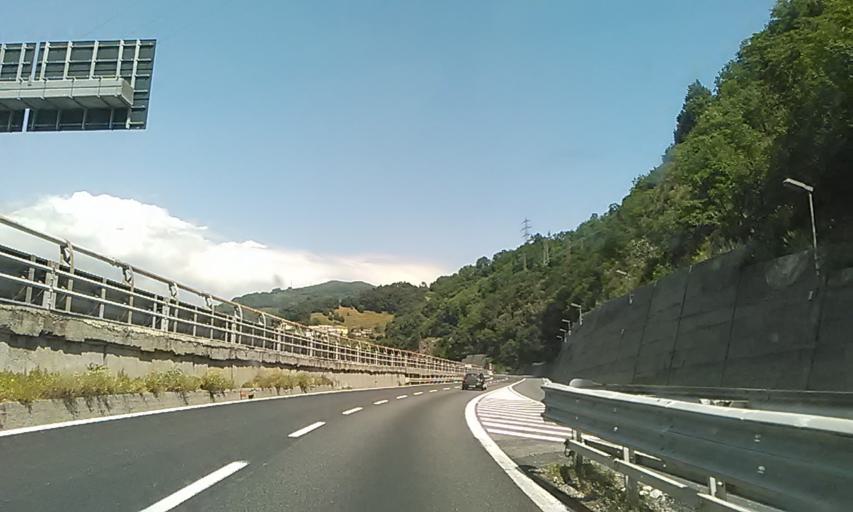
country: IT
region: Liguria
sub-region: Provincia di Genova
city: Mele
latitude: 44.4357
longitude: 8.7381
